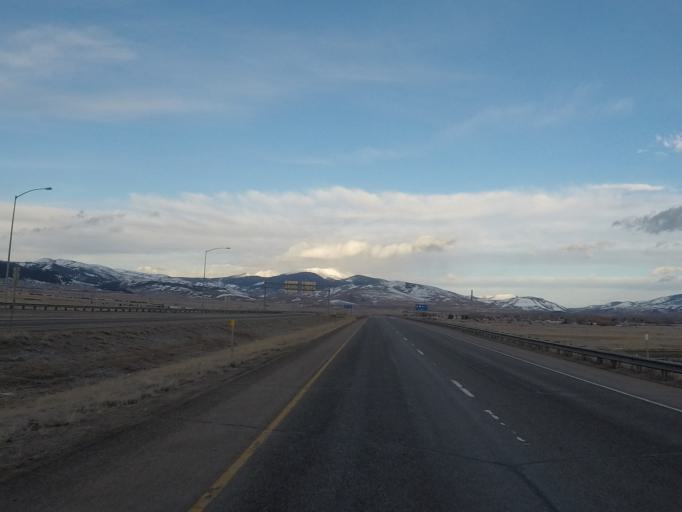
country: US
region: Montana
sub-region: Deer Lodge County
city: Warm Springs
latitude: 46.0955
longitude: -112.7964
